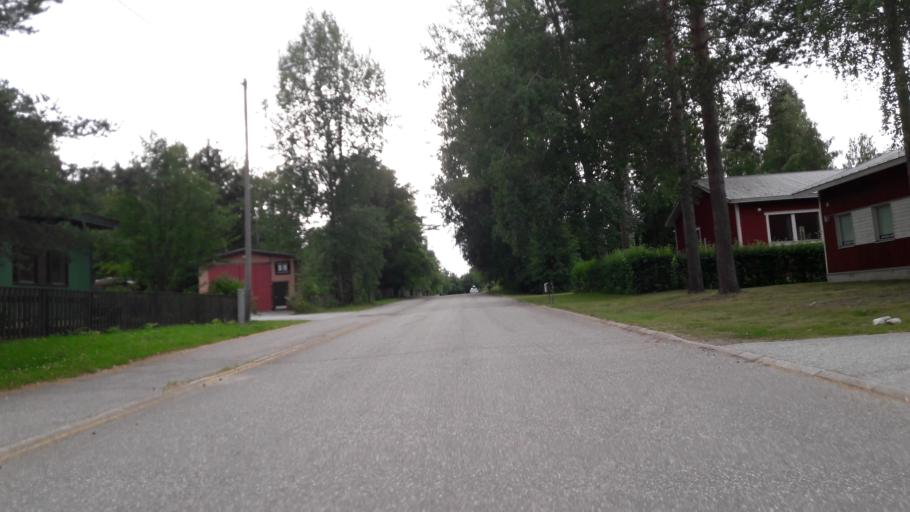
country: FI
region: North Karelia
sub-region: Joensuu
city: Joensuu
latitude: 62.5812
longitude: 29.8044
